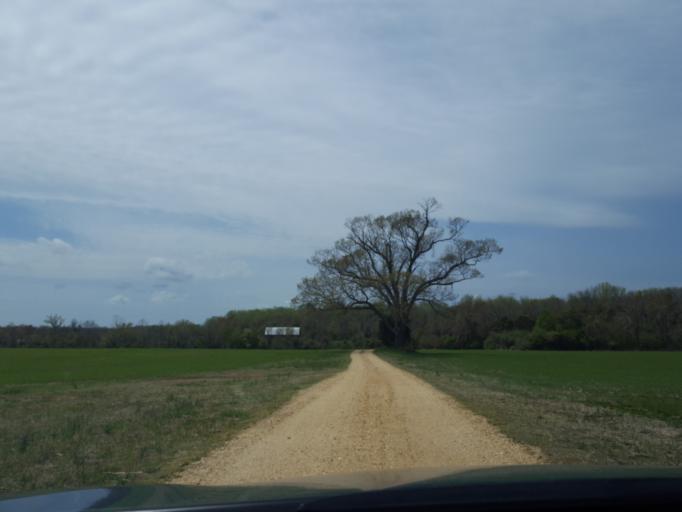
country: US
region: Maryland
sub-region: Calvert County
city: Dunkirk
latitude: 38.7327
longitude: -76.7022
